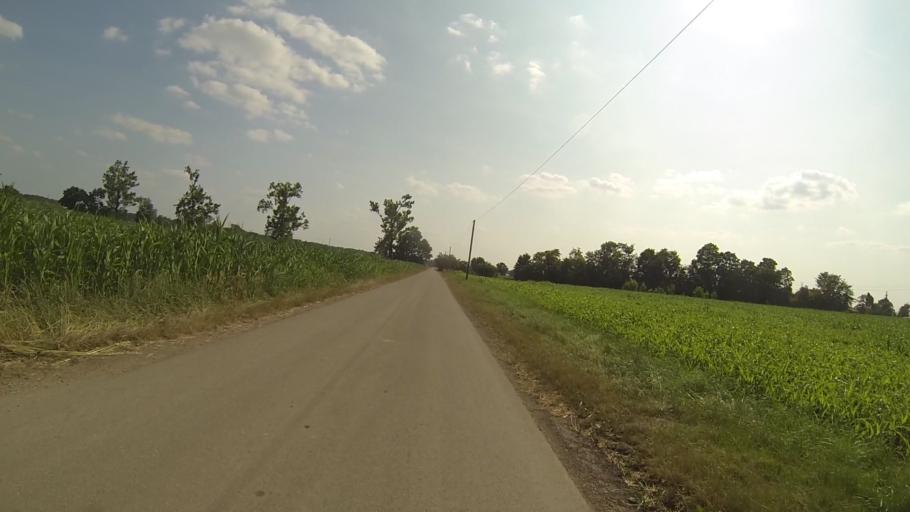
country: DE
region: Bavaria
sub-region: Swabia
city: Leipheim
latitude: 48.4656
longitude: 10.2068
